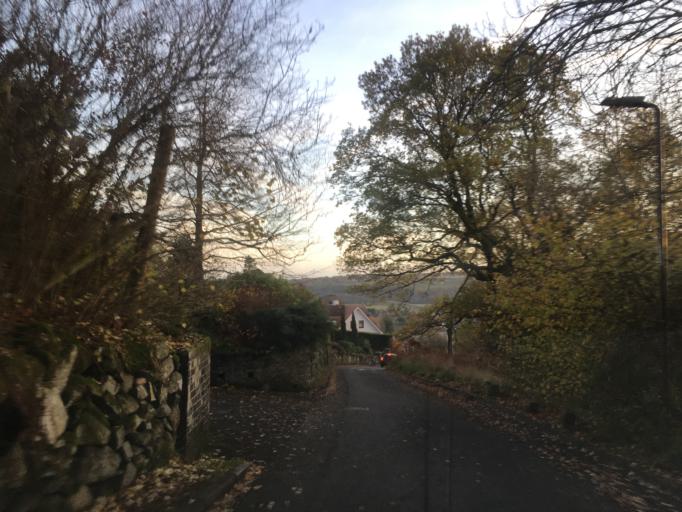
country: GB
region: Scotland
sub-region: Clackmannanshire
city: Dollar
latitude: 56.1707
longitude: -3.6698
